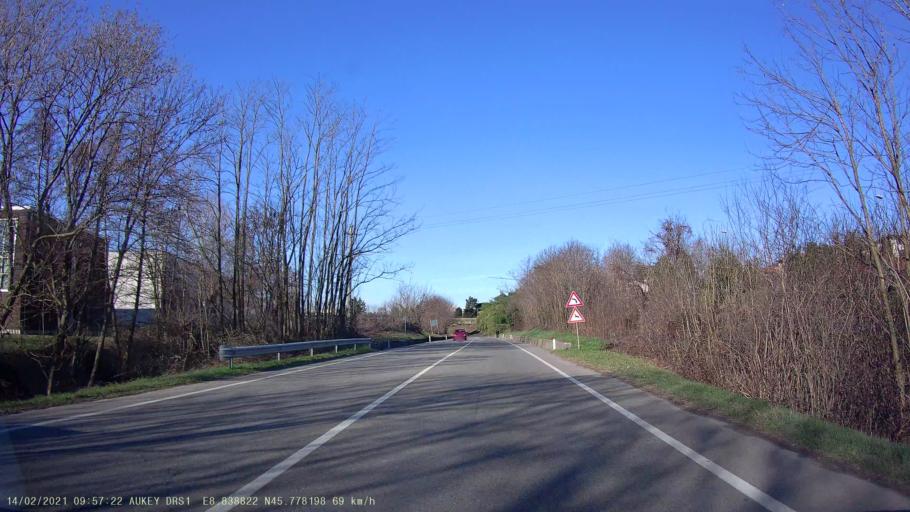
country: IT
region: Lombardy
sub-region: Provincia di Varese
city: Gazzada Schianno
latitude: 45.7783
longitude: 8.8381
